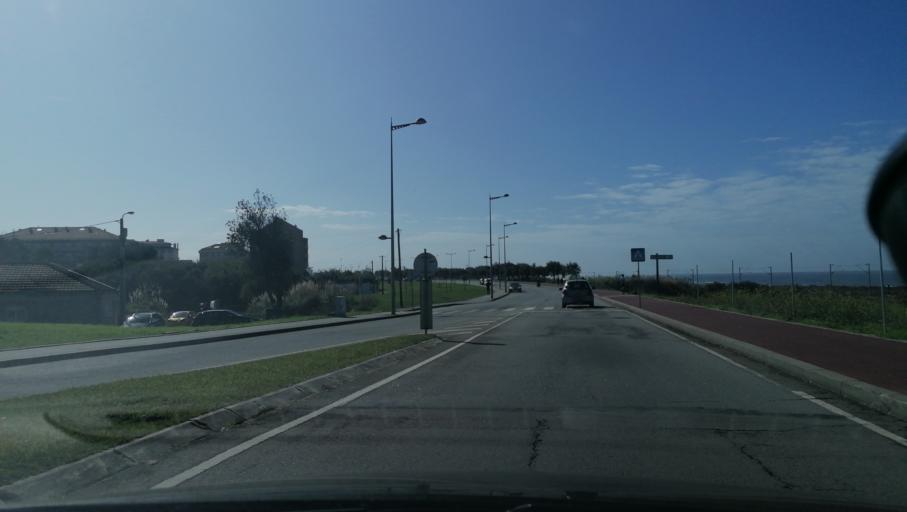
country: PT
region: Aveiro
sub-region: Espinho
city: Espinho
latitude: 41.0270
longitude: -8.6427
